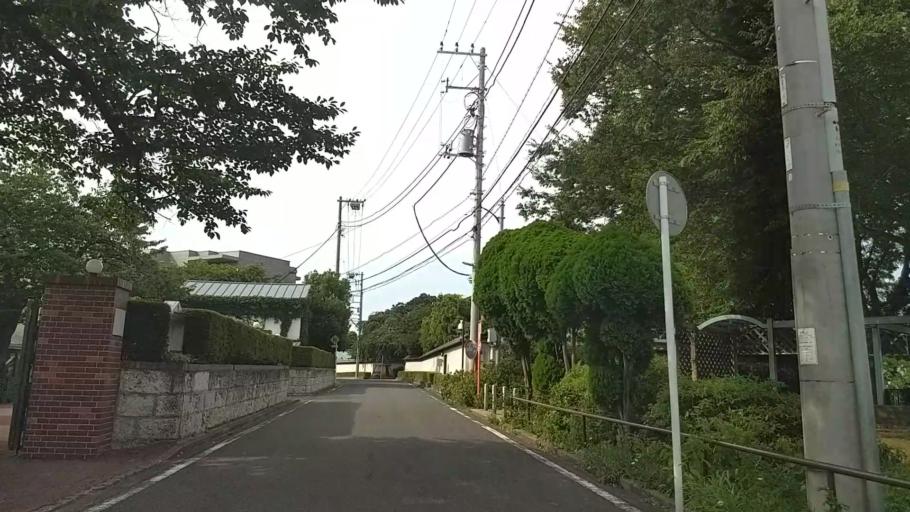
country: JP
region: Kanagawa
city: Yokohama
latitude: 35.4356
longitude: 139.6593
